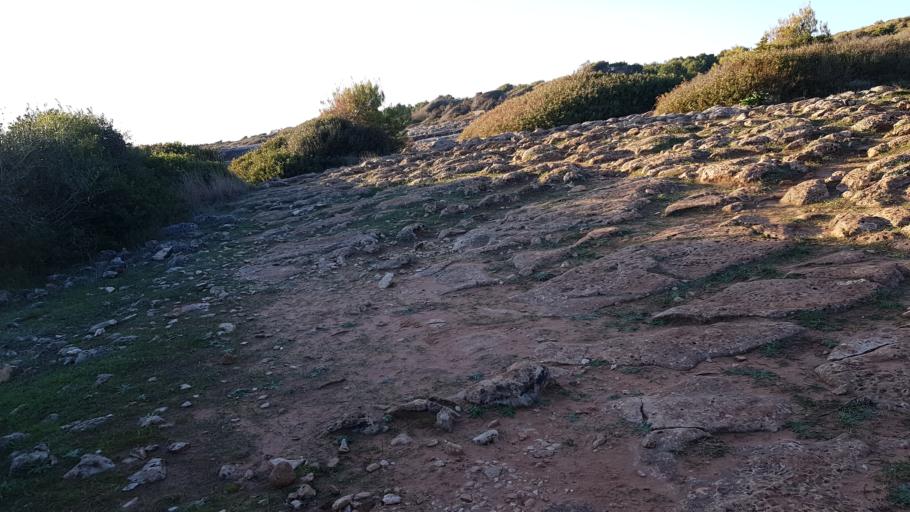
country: IT
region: Apulia
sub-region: Provincia di Lecce
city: Nardo
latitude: 40.1479
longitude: 17.9715
